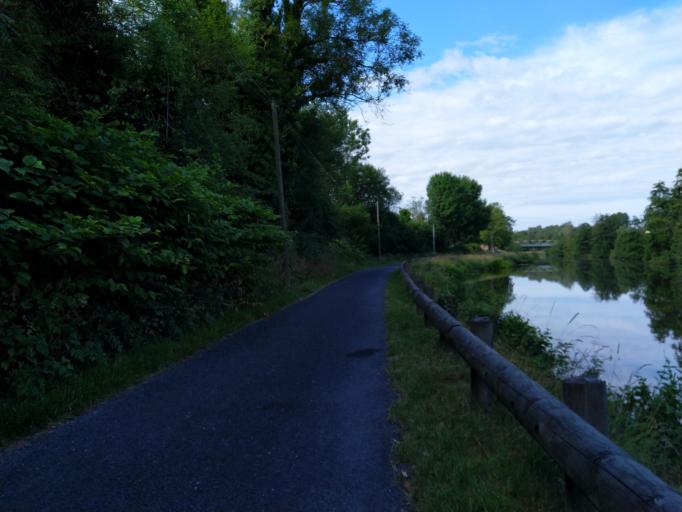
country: FR
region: Nord-Pas-de-Calais
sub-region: Departement du Nord
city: Marpent
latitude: 50.2958
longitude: 4.0797
